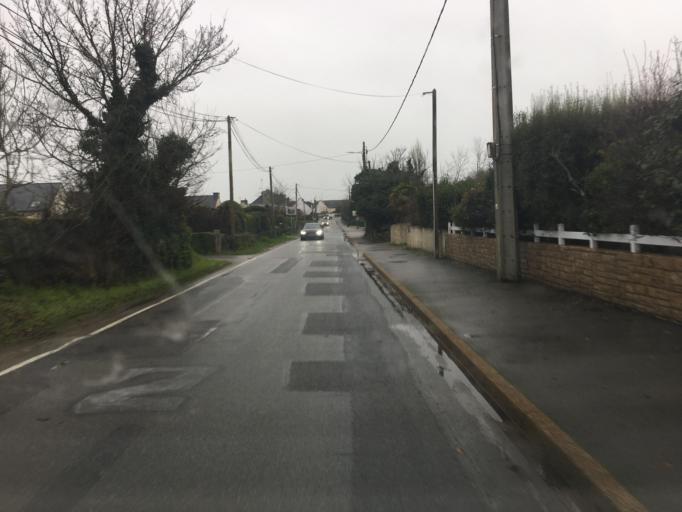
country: FR
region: Brittany
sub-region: Departement du Morbihan
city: Sarzeau
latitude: 47.5011
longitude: -2.6828
